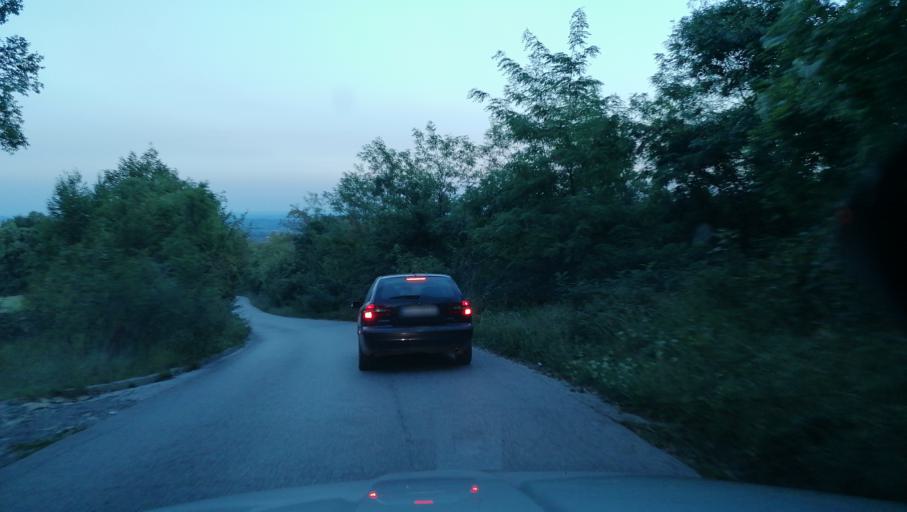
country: RS
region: Central Serbia
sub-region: Kolubarski Okrug
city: Valjevo
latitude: 44.2449
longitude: 19.8666
